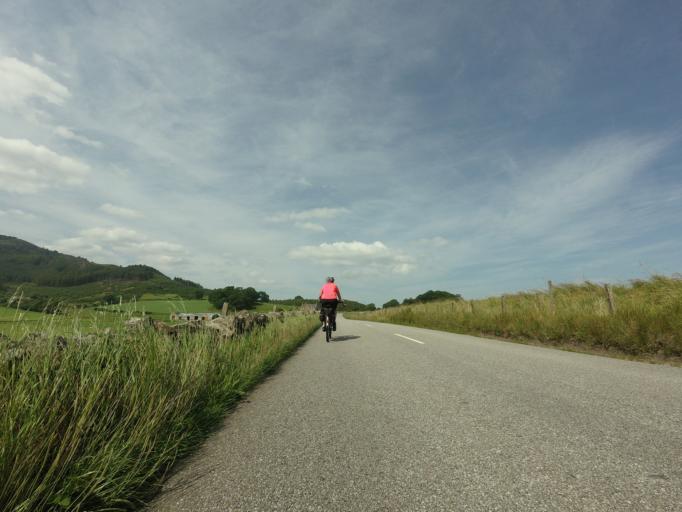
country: GB
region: Scotland
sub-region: Highland
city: Tain
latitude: 57.8476
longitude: -4.2013
